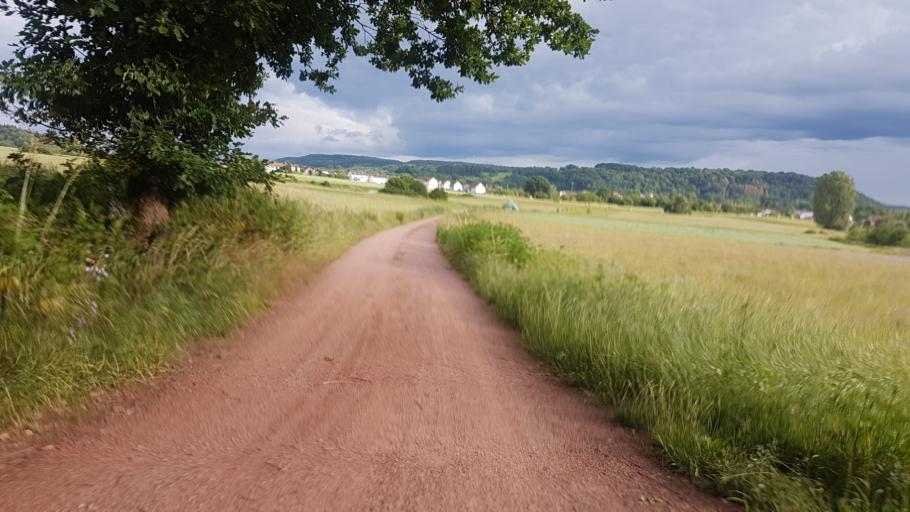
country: DE
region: Saarland
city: Britten
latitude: 49.4888
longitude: 6.7025
